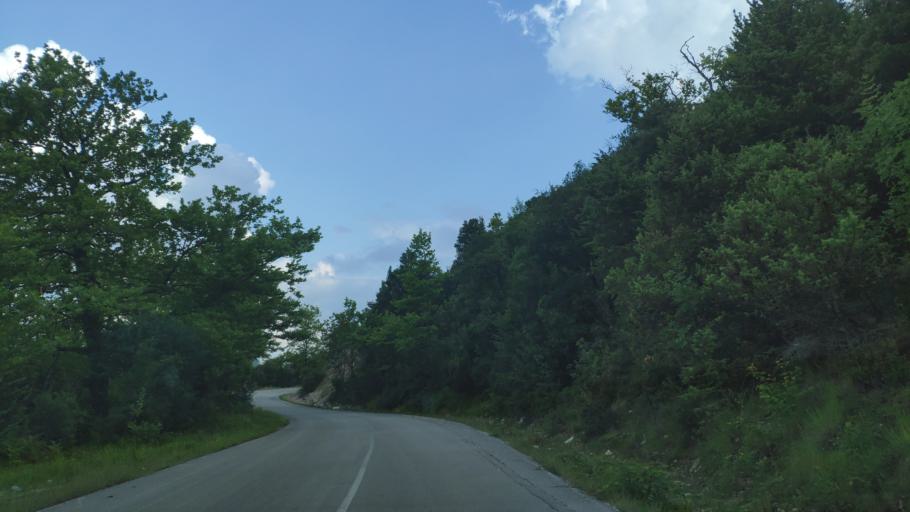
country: GR
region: Epirus
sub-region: Nomos Artas
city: Agios Dimitrios
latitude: 39.4294
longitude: 21.0160
